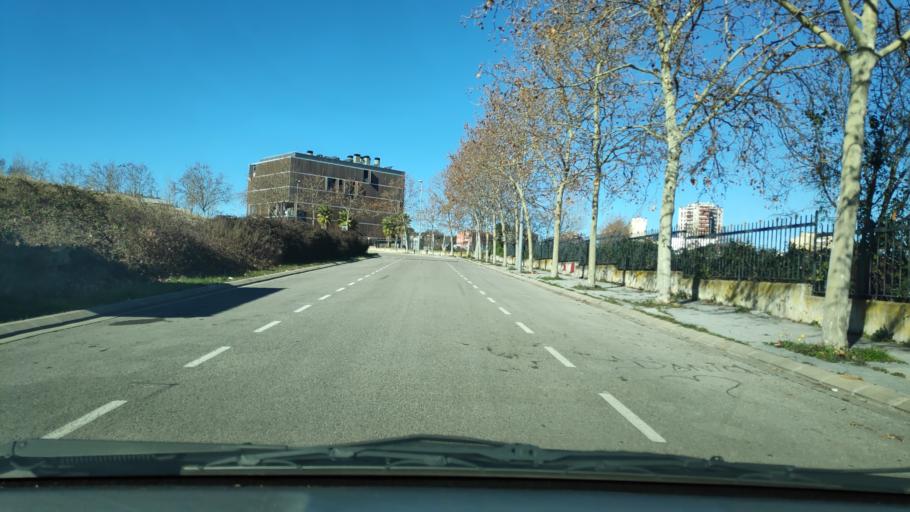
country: ES
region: Catalonia
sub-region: Provincia de Barcelona
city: Sant Quirze del Valles
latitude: 41.5393
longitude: 2.0908
